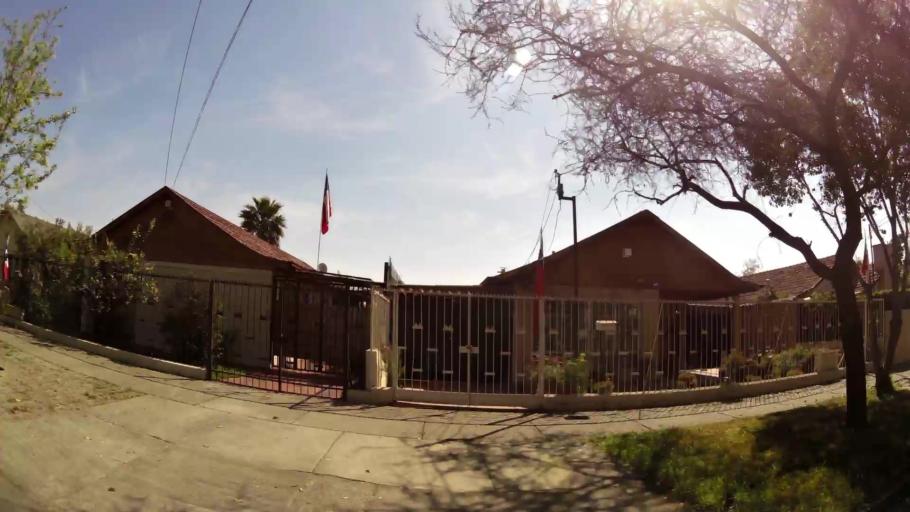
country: CL
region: Santiago Metropolitan
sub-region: Provincia de Santiago
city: Villa Presidente Frei, Nunoa, Santiago, Chile
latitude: -33.4891
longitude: -70.5870
